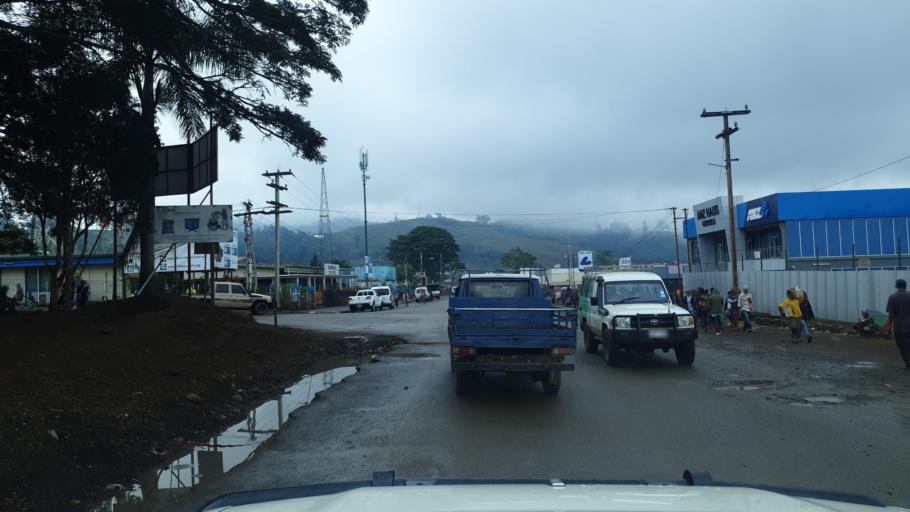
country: PG
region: Eastern Highlands
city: Goroka
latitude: -6.0733
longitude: 145.3916
